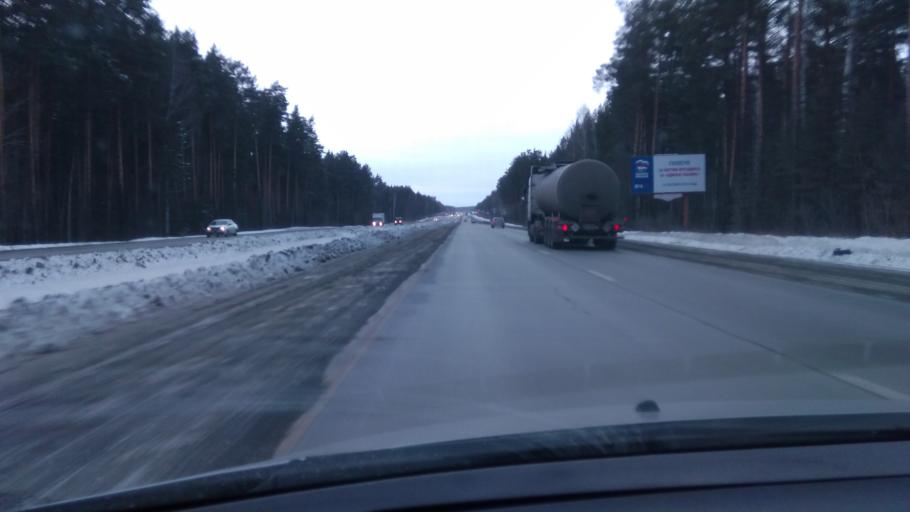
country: RU
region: Sverdlovsk
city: Sysert'
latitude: 56.5808
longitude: 60.8555
